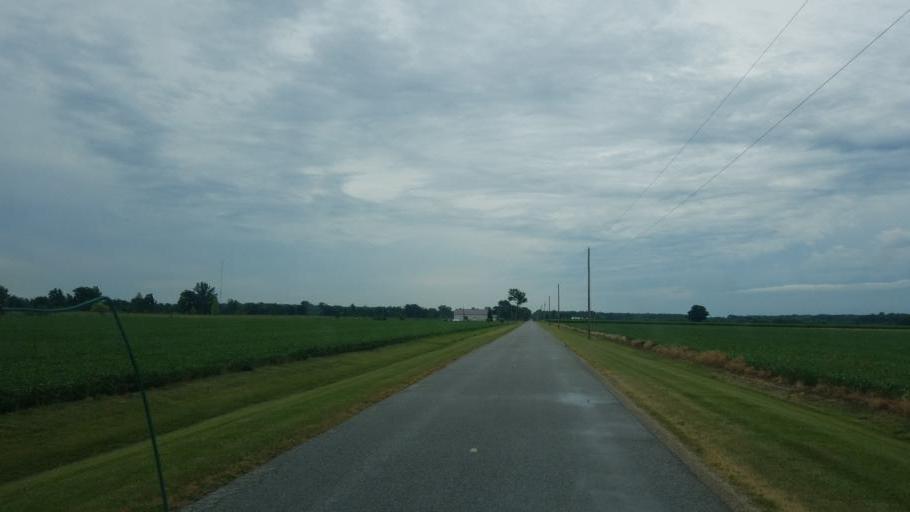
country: US
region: Ohio
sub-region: Defiance County
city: Hicksville
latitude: 41.2519
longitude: -84.6894
